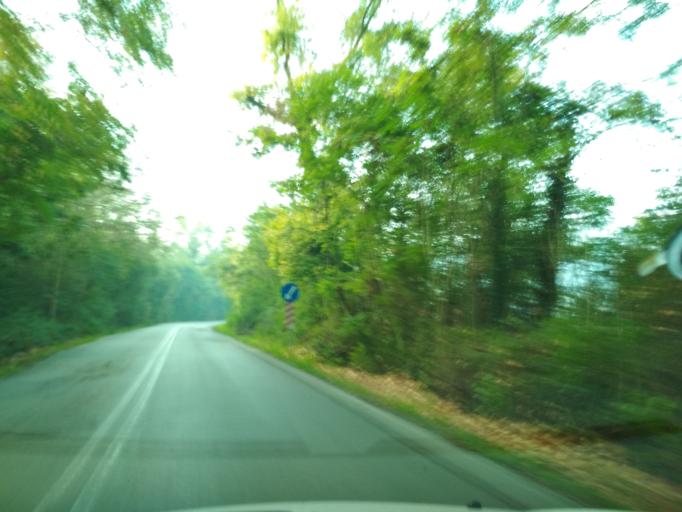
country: GR
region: Central Greece
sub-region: Nomos Evvoias
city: Prokopion
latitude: 38.7452
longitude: 23.4888
